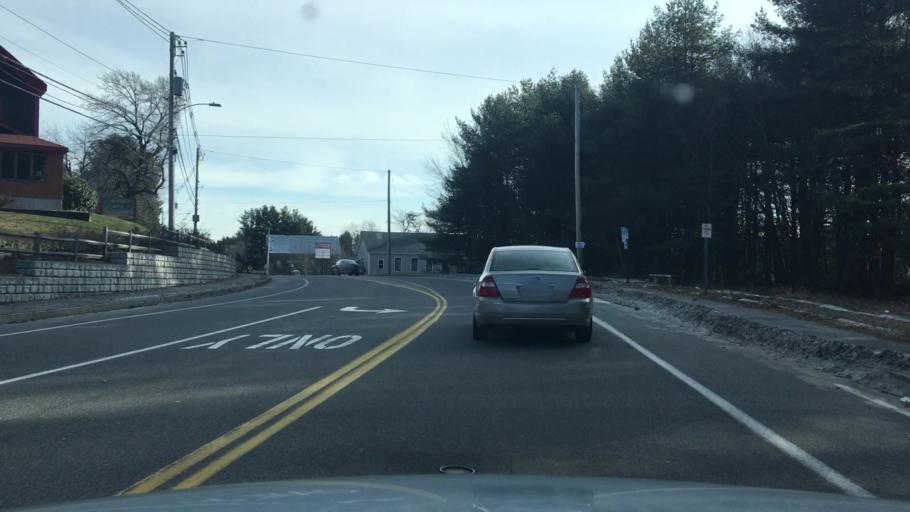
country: US
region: Maine
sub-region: Cumberland County
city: Westbrook
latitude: 43.7004
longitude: -70.3201
